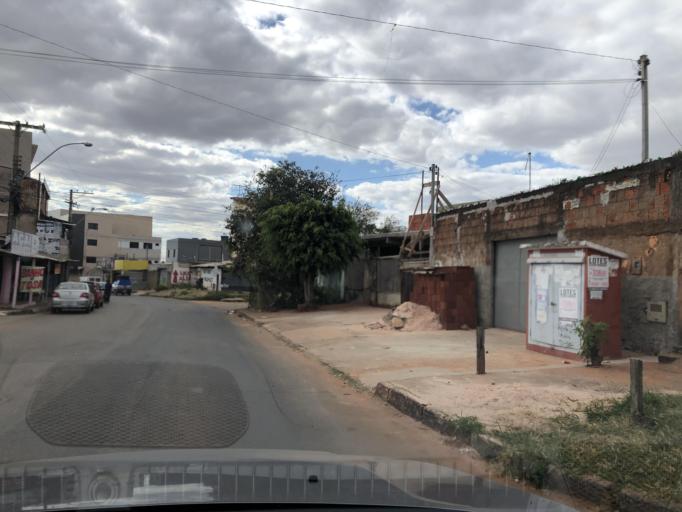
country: BR
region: Federal District
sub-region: Brasilia
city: Brasilia
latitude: -15.8810
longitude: -48.1119
